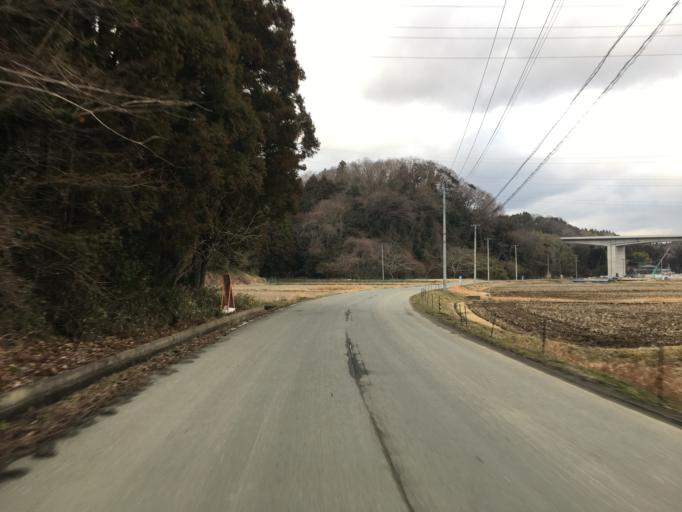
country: JP
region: Fukushima
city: Iwaki
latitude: 36.9399
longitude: 140.7908
